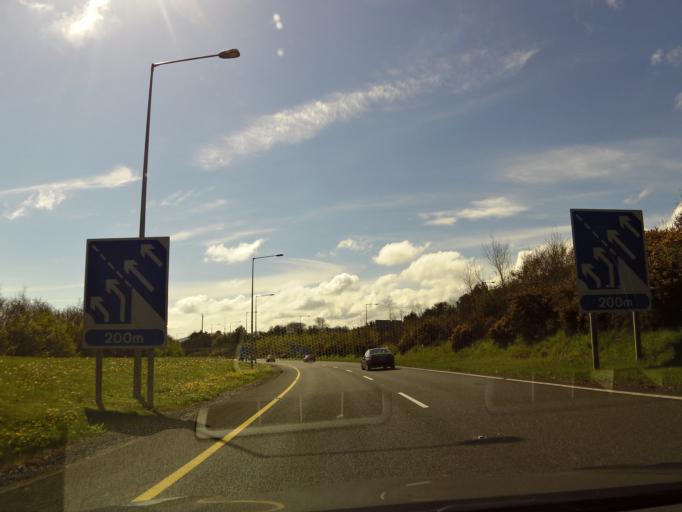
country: IE
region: Leinster
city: Shankill
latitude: 53.2328
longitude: -6.1315
